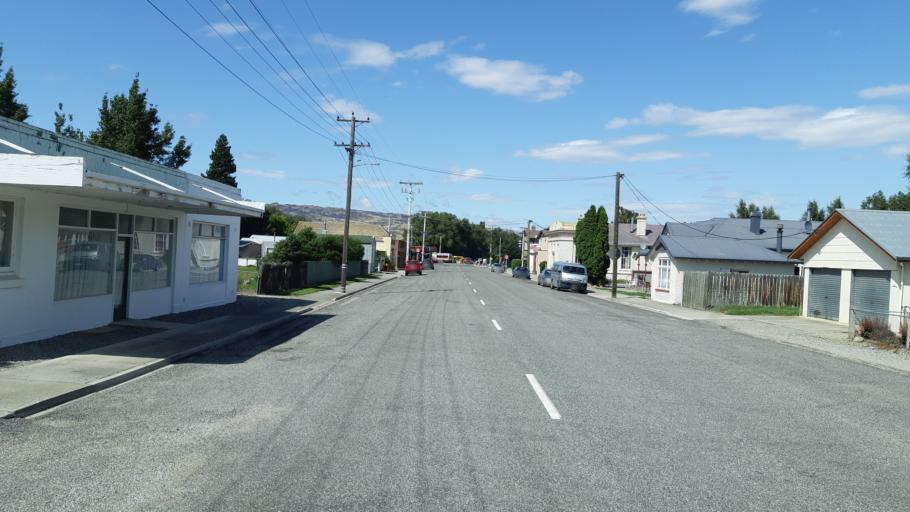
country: NZ
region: Otago
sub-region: Queenstown-Lakes District
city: Wanaka
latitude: -45.0926
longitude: 169.6019
